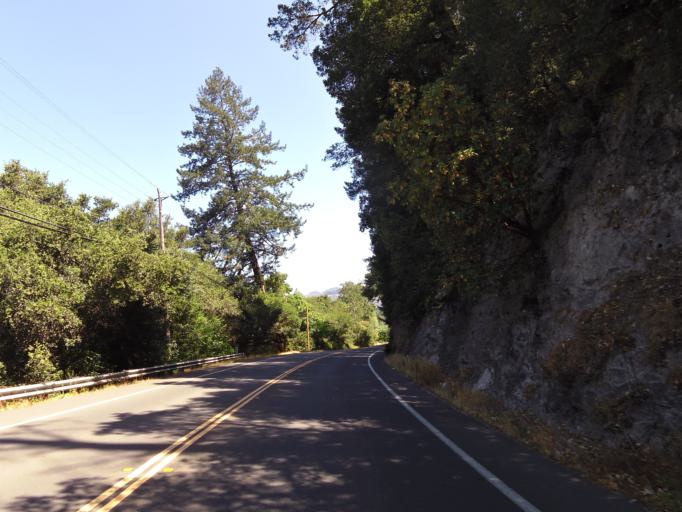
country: US
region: California
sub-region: Napa County
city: Deer Park
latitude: 38.5335
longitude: -122.4908
